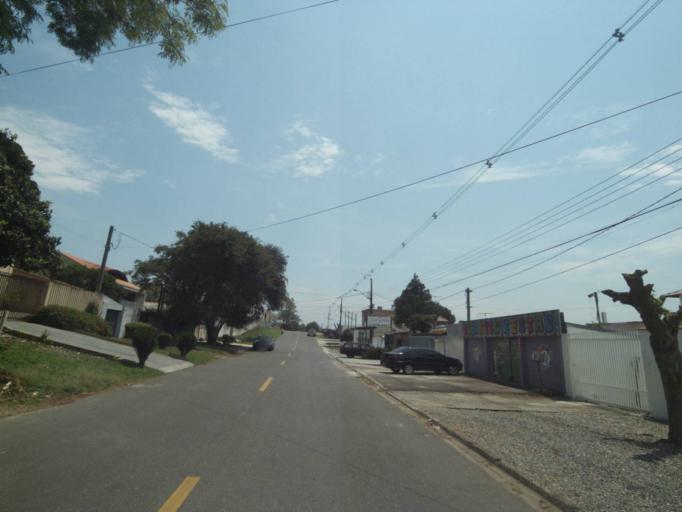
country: BR
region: Parana
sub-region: Pinhais
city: Pinhais
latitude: -25.4104
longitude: -49.2060
